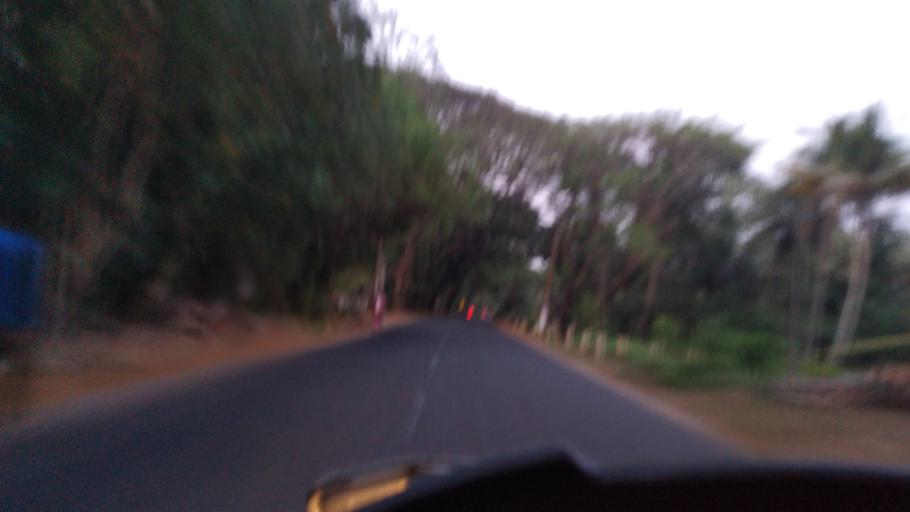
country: IN
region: Kerala
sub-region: Kottayam
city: Kottayam
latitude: 9.6045
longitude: 76.4330
